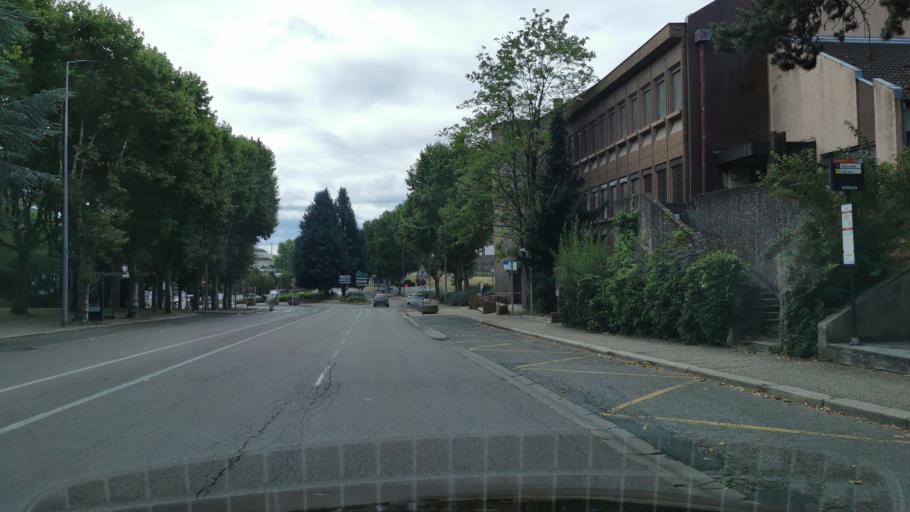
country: FR
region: Bourgogne
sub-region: Departement de Saone-et-Loire
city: Le Creusot
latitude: 46.8069
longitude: 4.4328
